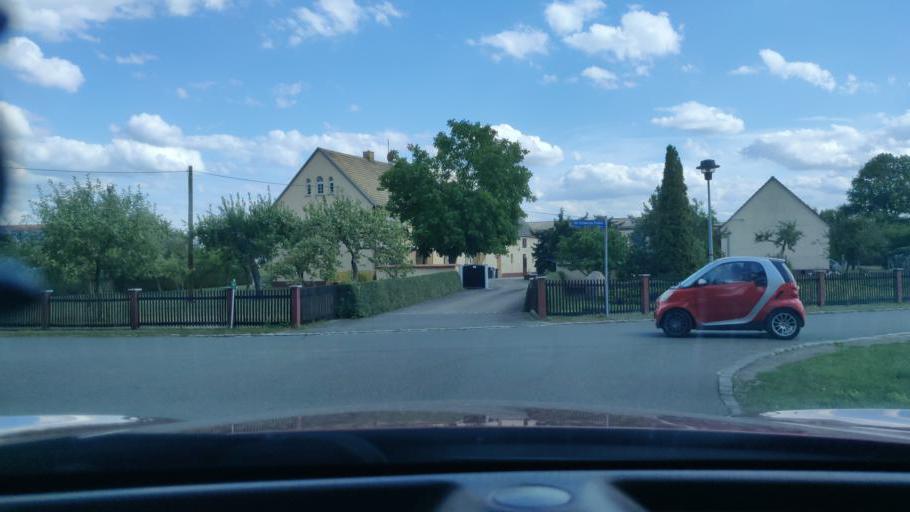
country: DE
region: Saxony
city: Mockrehna
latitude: 51.5005
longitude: 12.8434
